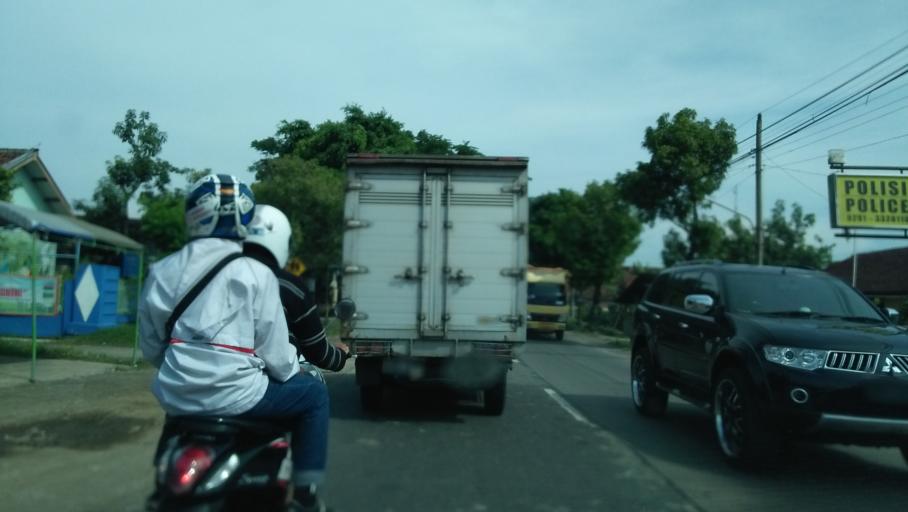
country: ID
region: Central Java
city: Welahan
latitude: -6.7956
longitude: 110.7259
